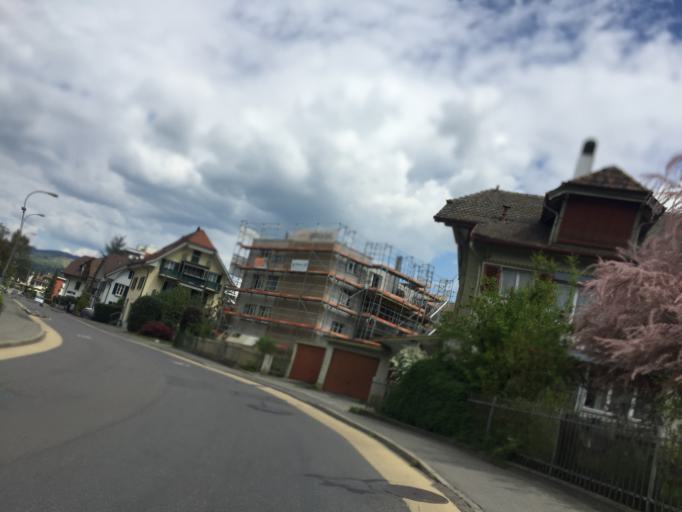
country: CH
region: Bern
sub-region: Thun District
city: Thun
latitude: 46.7624
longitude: 7.6198
